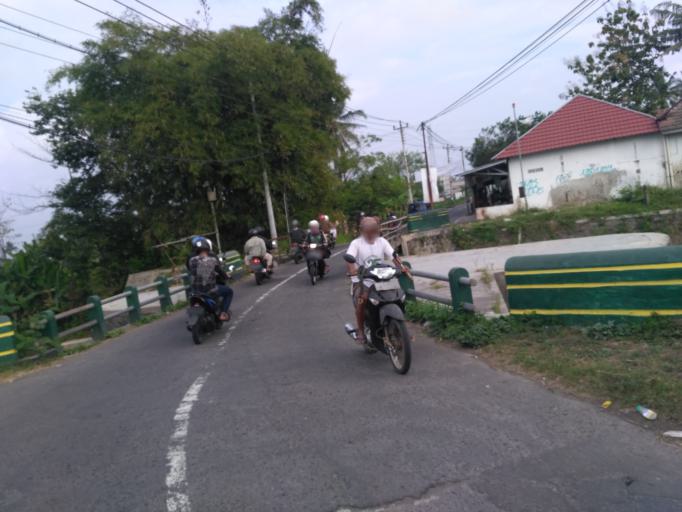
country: ID
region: Daerah Istimewa Yogyakarta
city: Melati
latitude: -7.7102
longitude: 110.3906
